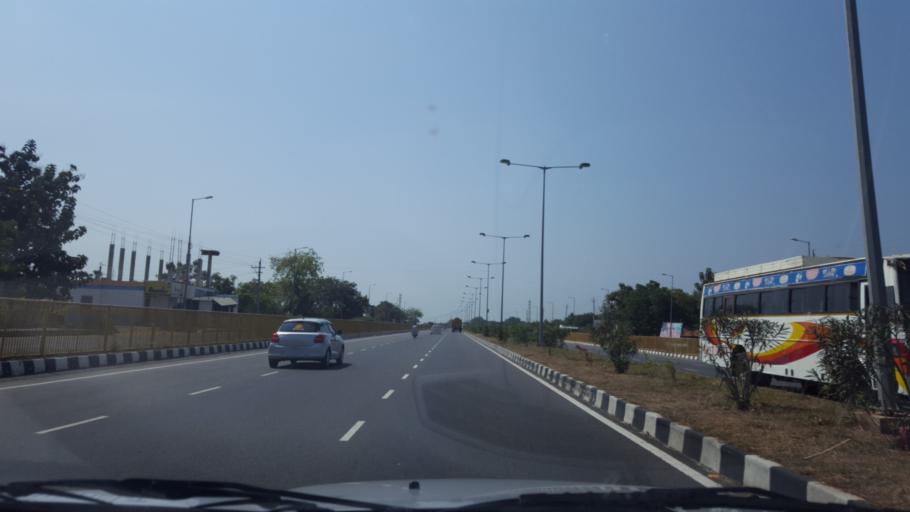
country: IN
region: Andhra Pradesh
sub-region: Prakasam
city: pedda nakkalapalem
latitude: 15.9586
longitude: 80.0897
